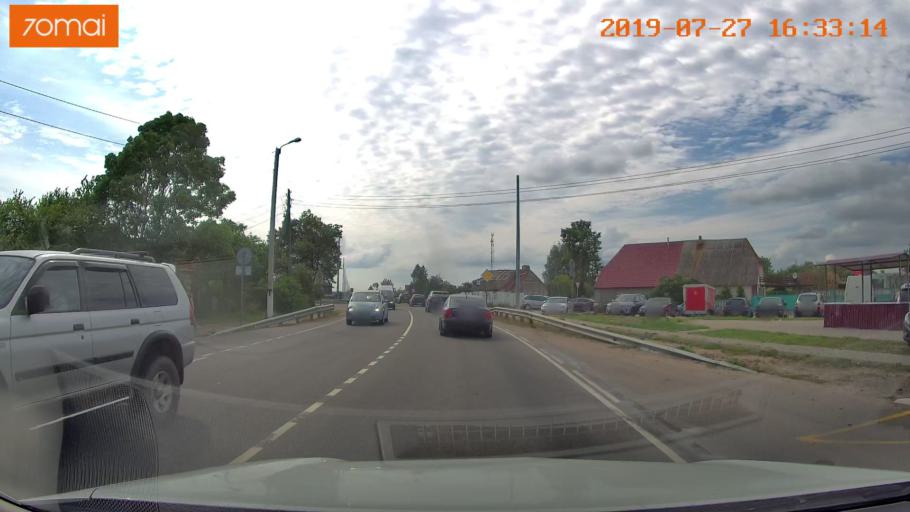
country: RU
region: Kaliningrad
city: Gvardeysk
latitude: 54.6507
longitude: 21.3406
